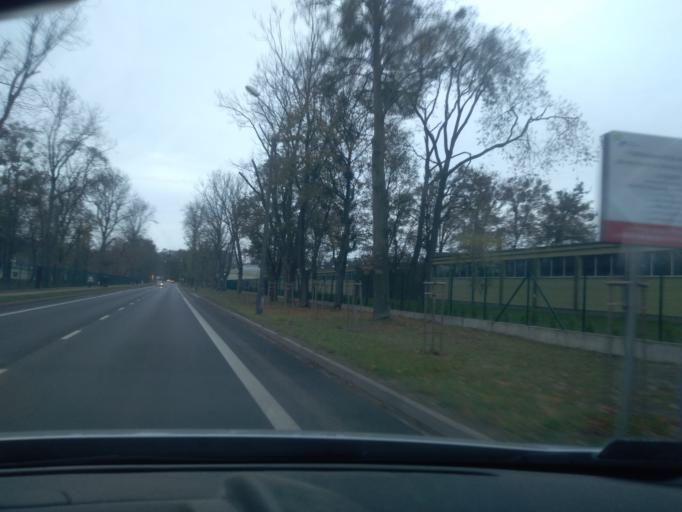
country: PL
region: Greater Poland Voivodeship
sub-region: Powiat poznanski
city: Murowana Goslina
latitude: 52.5387
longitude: 16.9442
